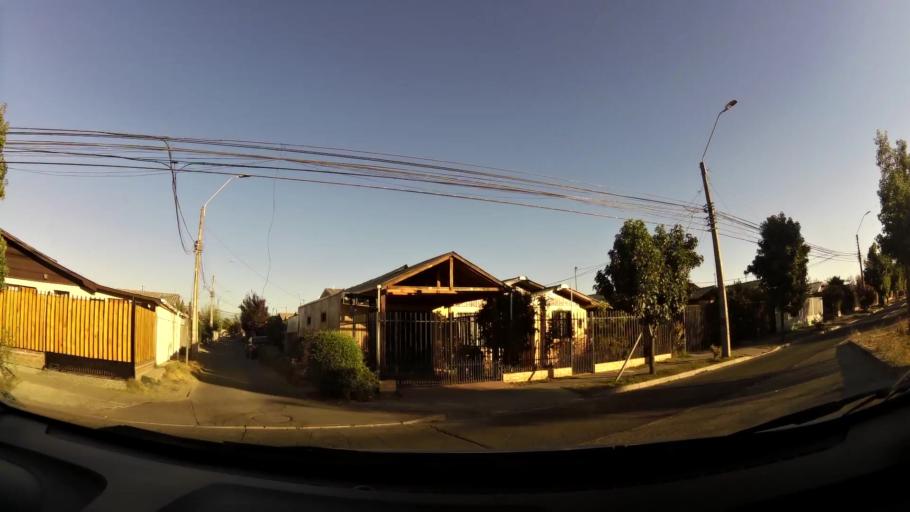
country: CL
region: O'Higgins
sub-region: Provincia de Cachapoal
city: Rancagua
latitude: -34.1749
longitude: -70.7640
